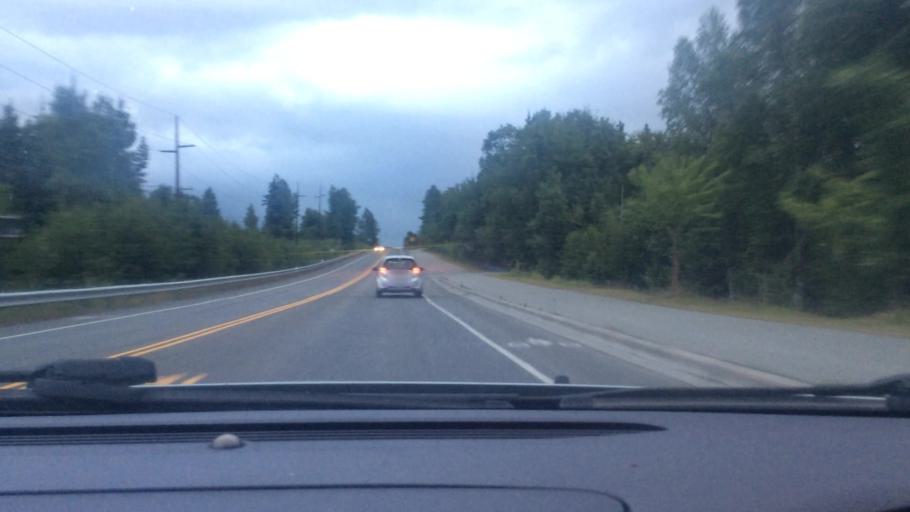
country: US
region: Alaska
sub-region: Anchorage Municipality
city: Anchorage
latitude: 61.1503
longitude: -149.8042
